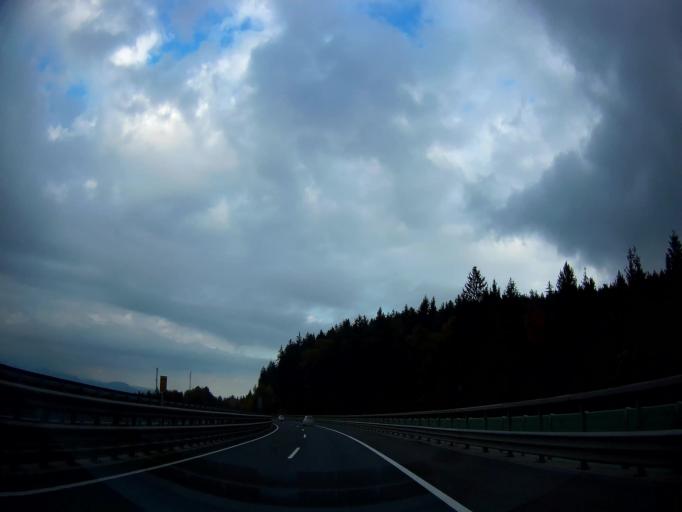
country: AT
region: Styria
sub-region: Politischer Bezirk Voitsberg
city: Ligist
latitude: 46.9746
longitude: 15.1894
